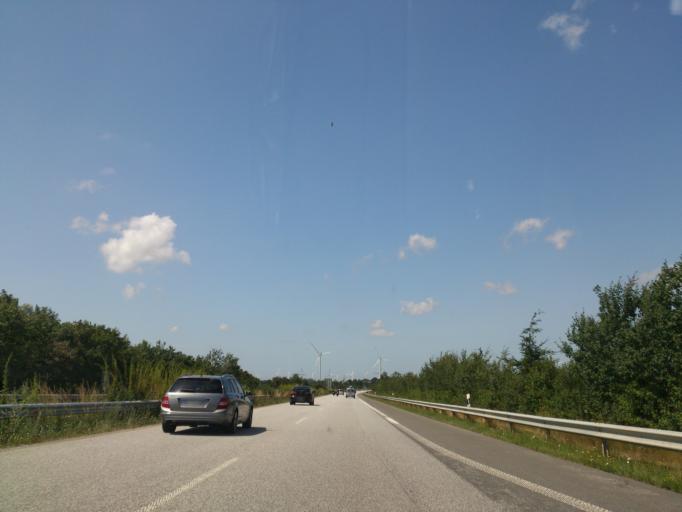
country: DE
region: Schleswig-Holstein
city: Hemmingstedt
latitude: 54.1697
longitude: 9.0835
